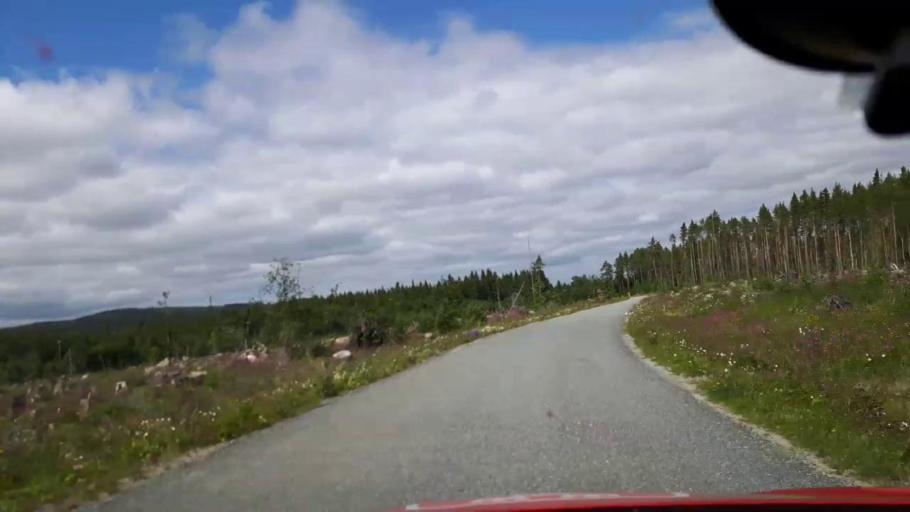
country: SE
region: Jaemtland
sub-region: Braecke Kommun
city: Braecke
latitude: 62.8361
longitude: 15.3057
